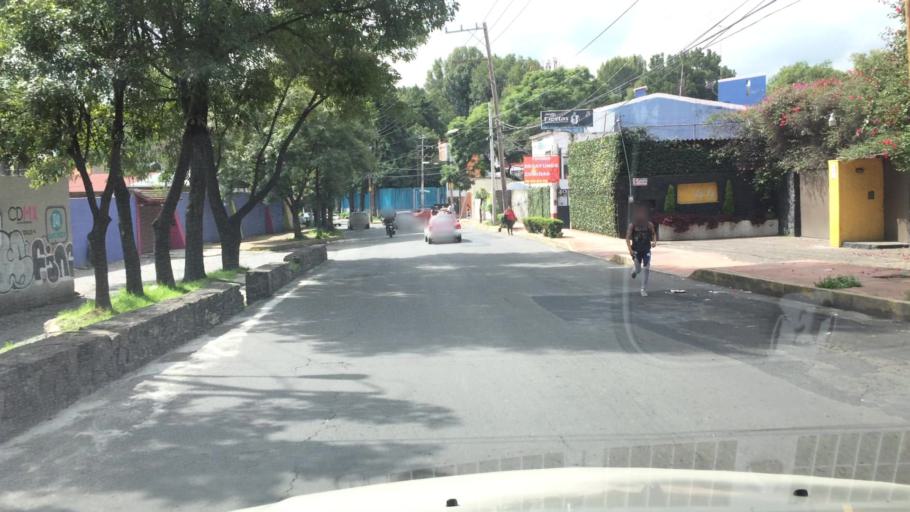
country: MX
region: Mexico City
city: Xochimilco
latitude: 19.2758
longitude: -99.1328
